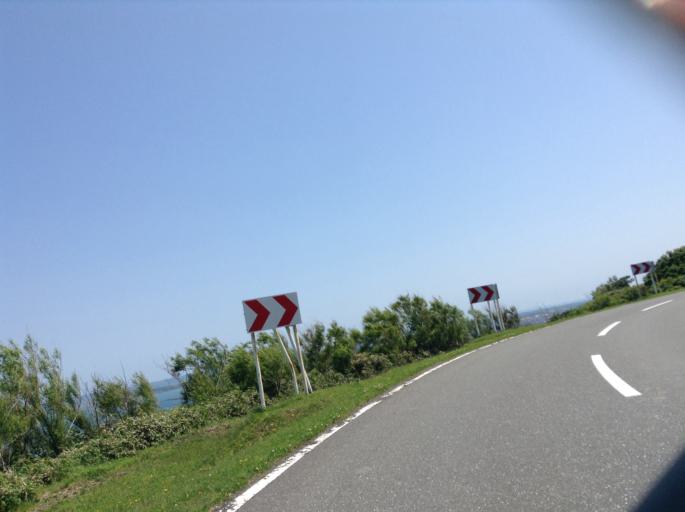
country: JP
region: Hokkaido
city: Wakkanai
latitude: 45.4194
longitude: 141.6697
